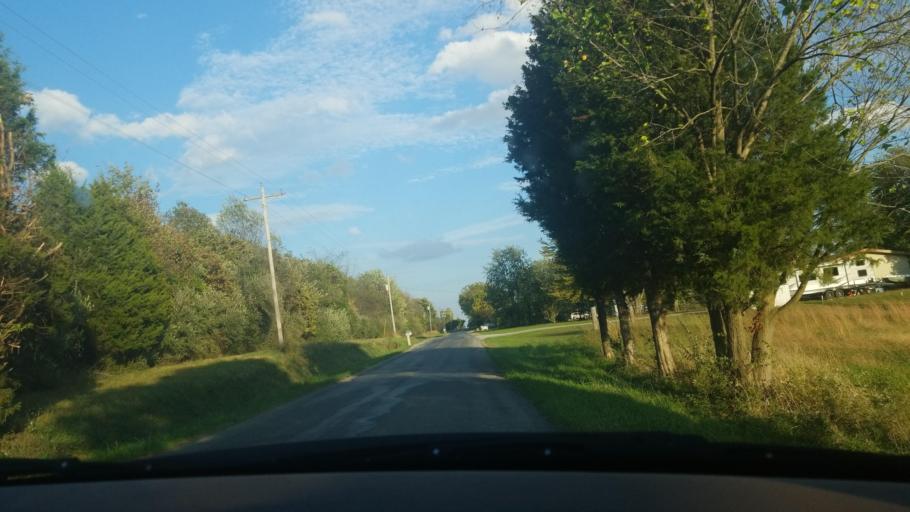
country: US
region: Illinois
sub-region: Saline County
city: Carrier Mills
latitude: 37.7719
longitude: -88.7334
